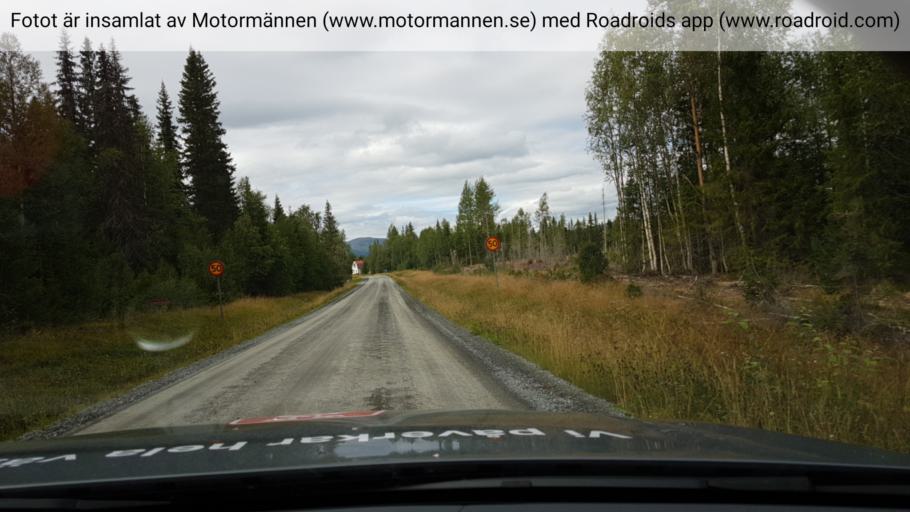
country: SE
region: Jaemtland
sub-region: Krokoms Kommun
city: Valla
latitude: 63.6914
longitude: 13.6695
